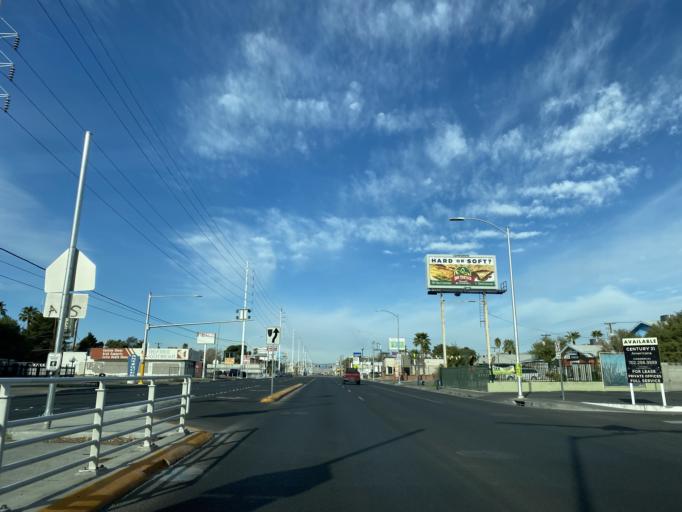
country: US
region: Nevada
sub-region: Clark County
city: Las Vegas
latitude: 36.1589
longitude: -115.1287
